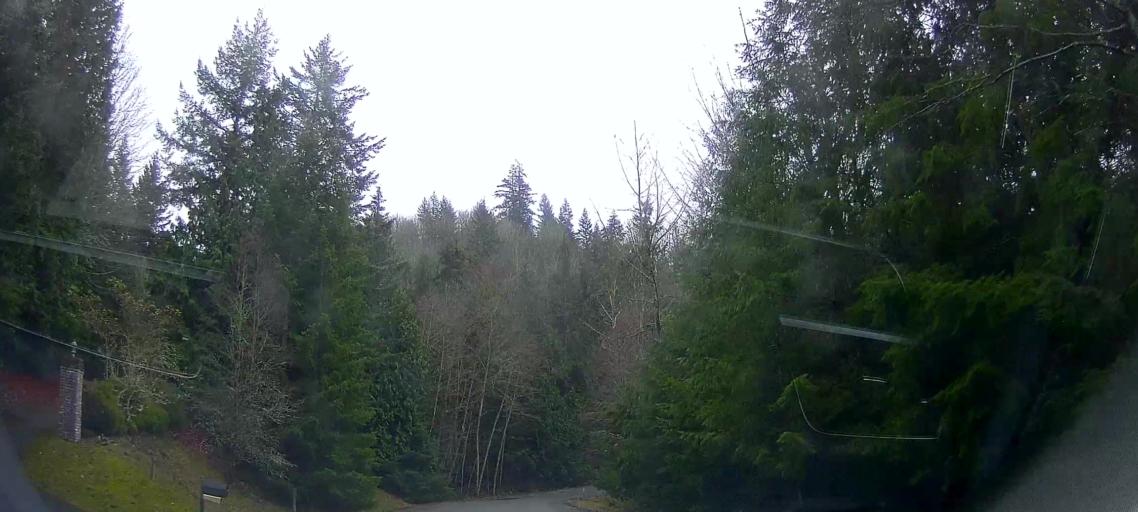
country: US
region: Washington
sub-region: Skagit County
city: Big Lake
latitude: 48.3823
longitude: -122.2914
